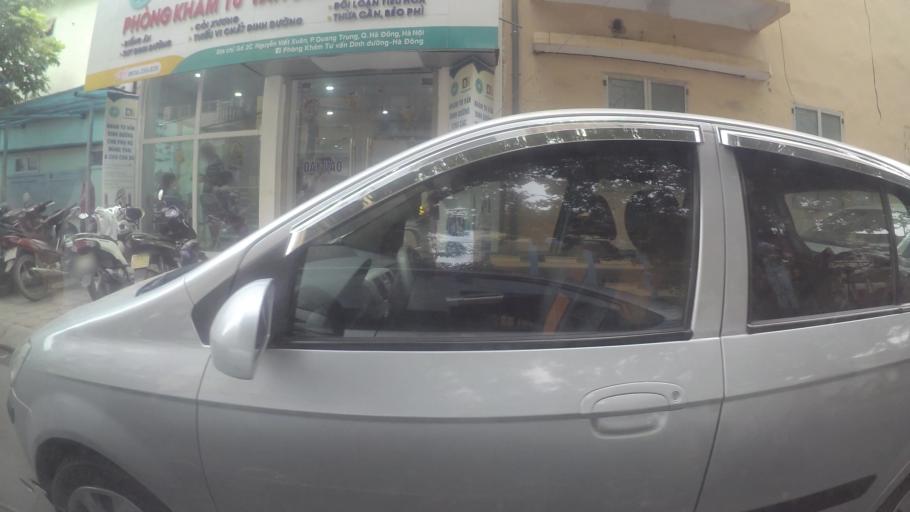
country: VN
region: Ha Noi
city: Ha Dong
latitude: 20.9705
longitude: 105.7736
